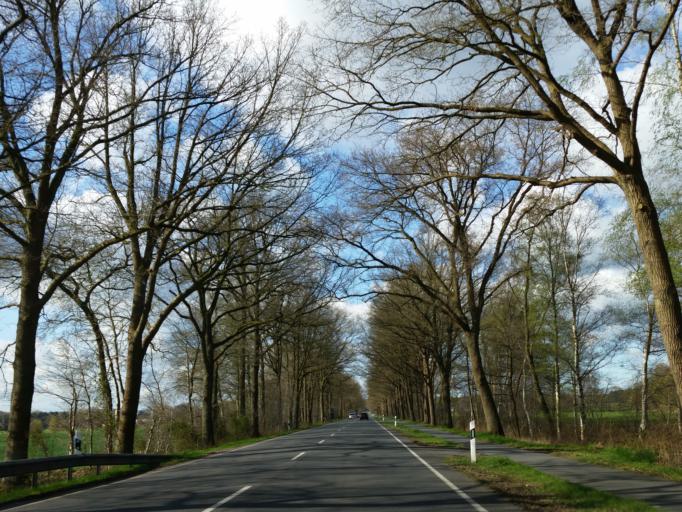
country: DE
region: Lower Saxony
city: Ahausen
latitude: 53.0521
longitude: 9.3329
